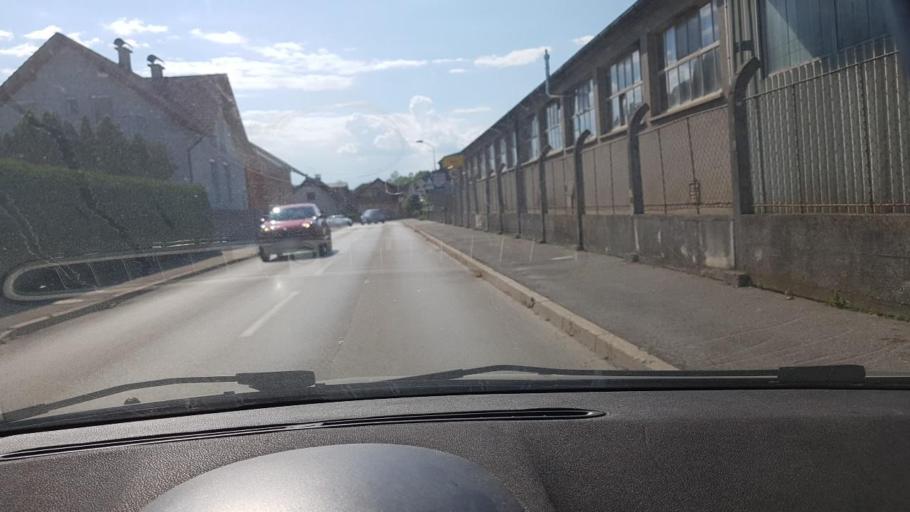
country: SI
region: Domzale
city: Vir
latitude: 46.1613
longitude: 14.6059
